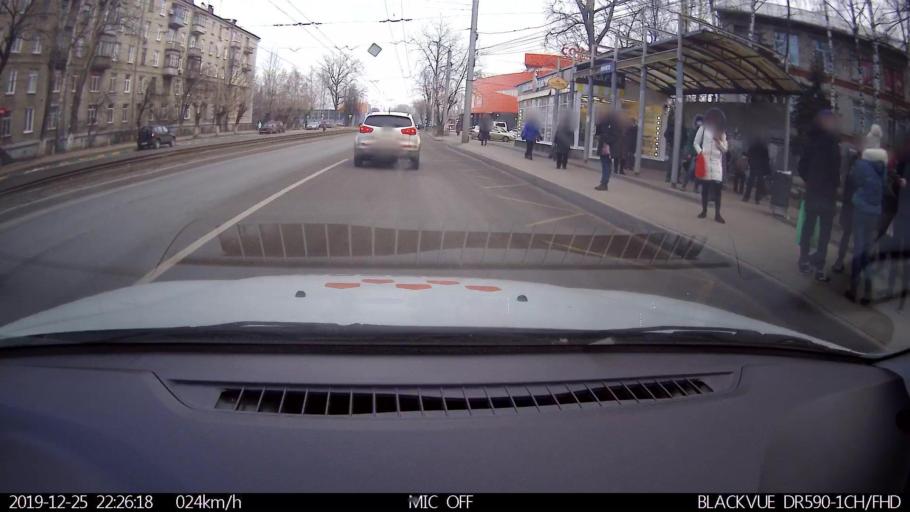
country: RU
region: Nizjnij Novgorod
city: Gorbatovka
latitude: 56.3297
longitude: 43.8539
